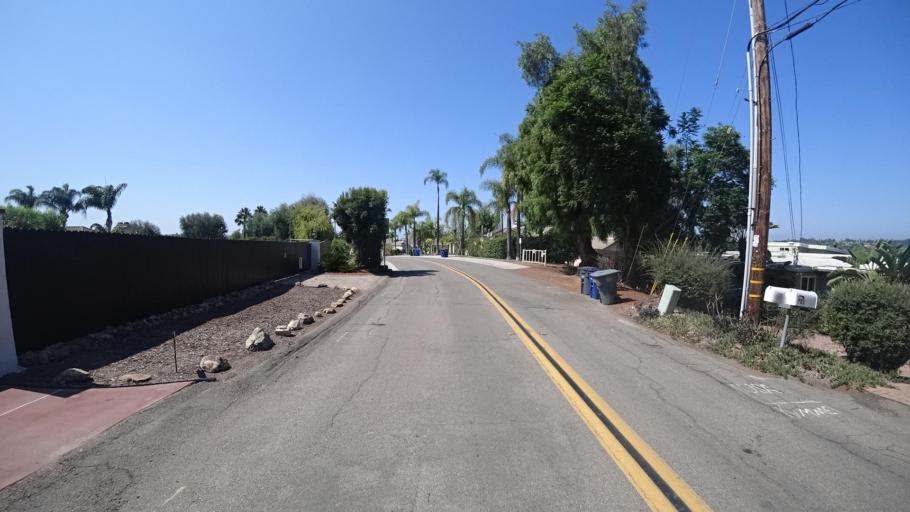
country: US
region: California
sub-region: San Diego County
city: Lake San Marcos
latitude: 33.1608
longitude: -117.2149
